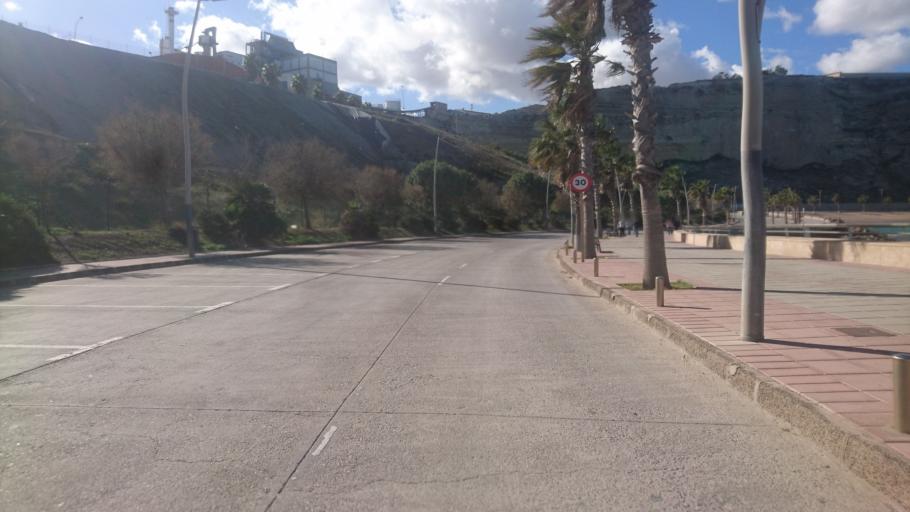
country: ES
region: Melilla
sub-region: Melilla
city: Melilla
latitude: 35.3031
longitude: -2.9393
